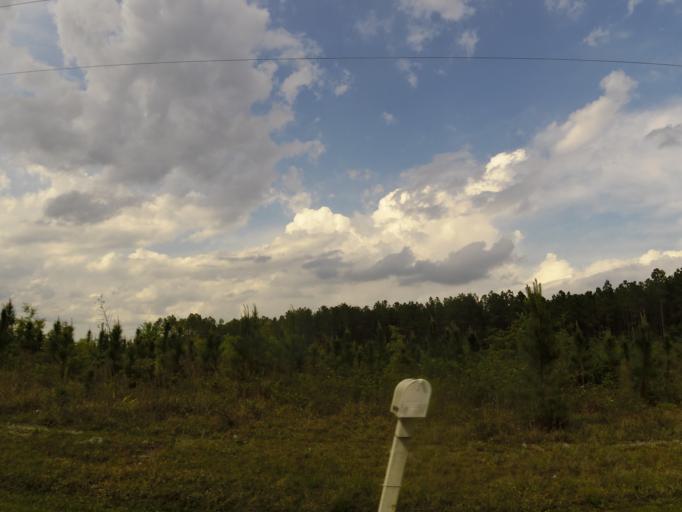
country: US
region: Georgia
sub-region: Charlton County
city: Folkston
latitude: 30.8079
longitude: -82.0504
